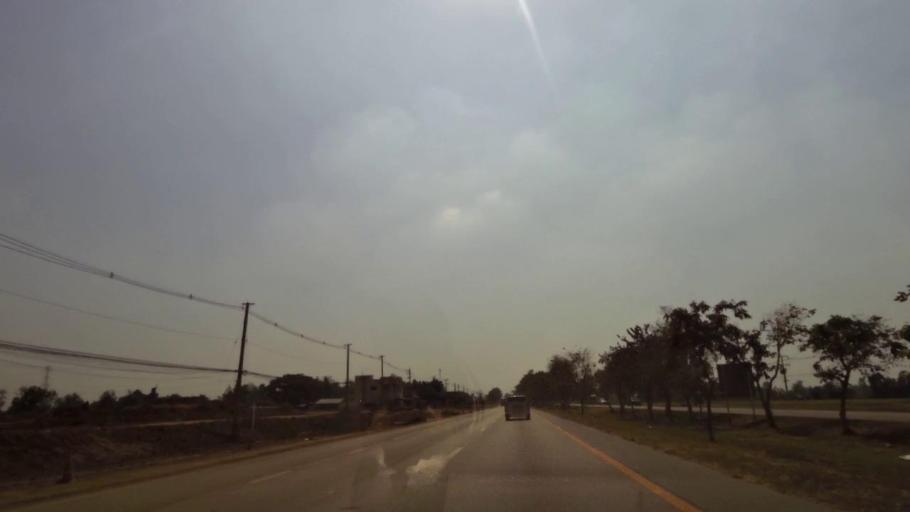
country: TH
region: Phichit
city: Wachira Barami
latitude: 16.5221
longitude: 100.1430
